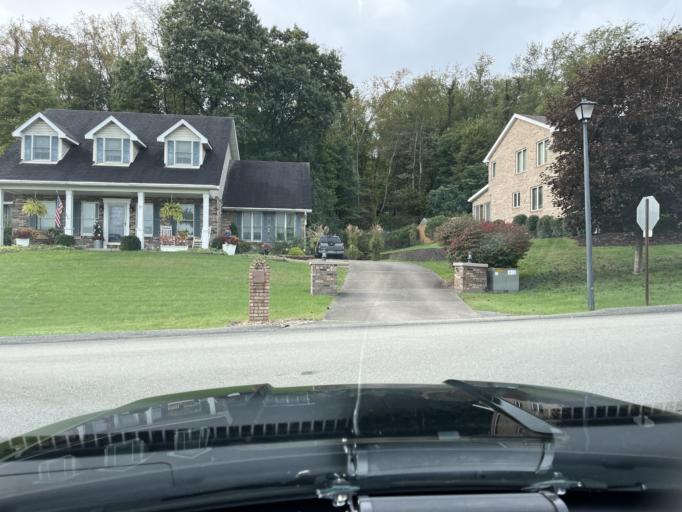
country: US
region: Pennsylvania
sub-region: Fayette County
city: Leith-Hatfield
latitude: 39.8843
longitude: -79.7308
